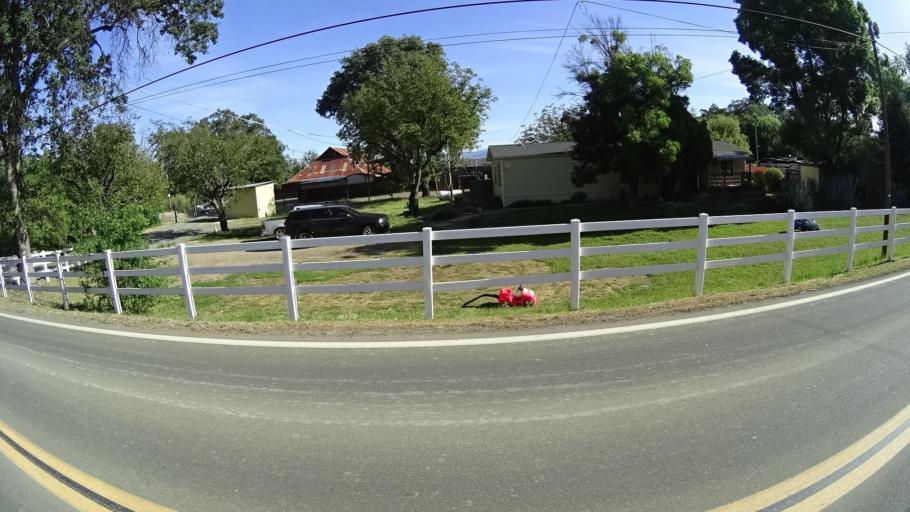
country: US
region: California
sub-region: Lake County
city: Kelseyville
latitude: 39.0149
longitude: -122.8704
